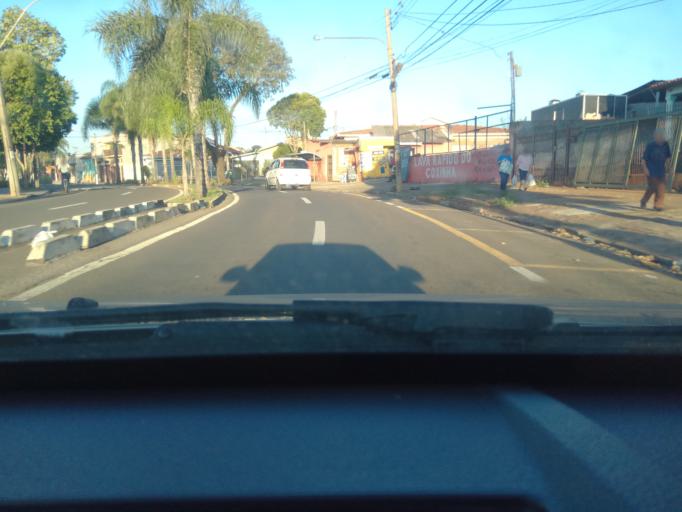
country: BR
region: Sao Paulo
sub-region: Piracicaba
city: Piracicaba
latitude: -22.7351
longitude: -47.6628
